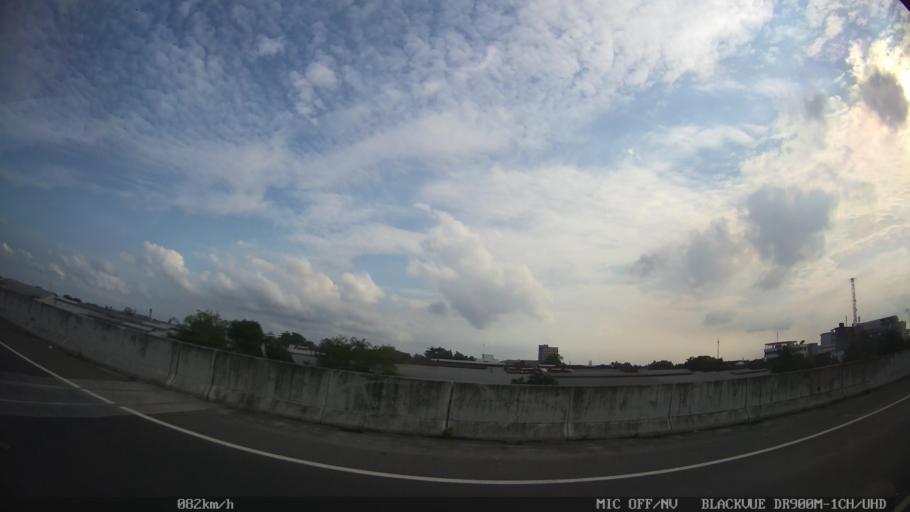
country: ID
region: North Sumatra
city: Medan
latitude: 3.6482
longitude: 98.6653
